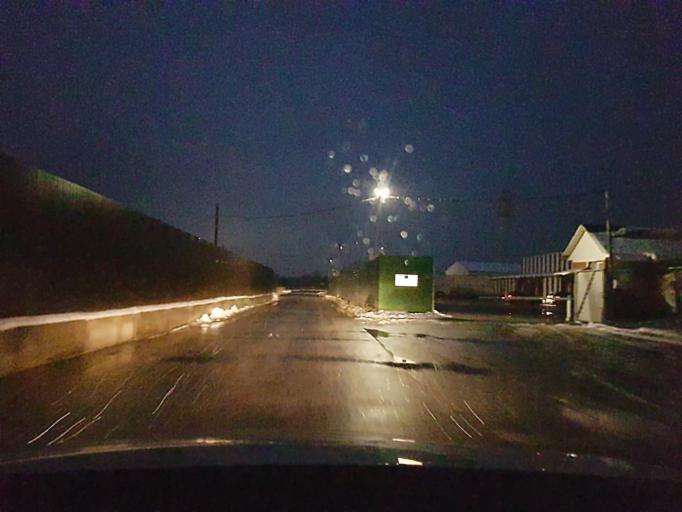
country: RU
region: Moskovskaya
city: Marfino
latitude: 56.0122
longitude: 37.5501
